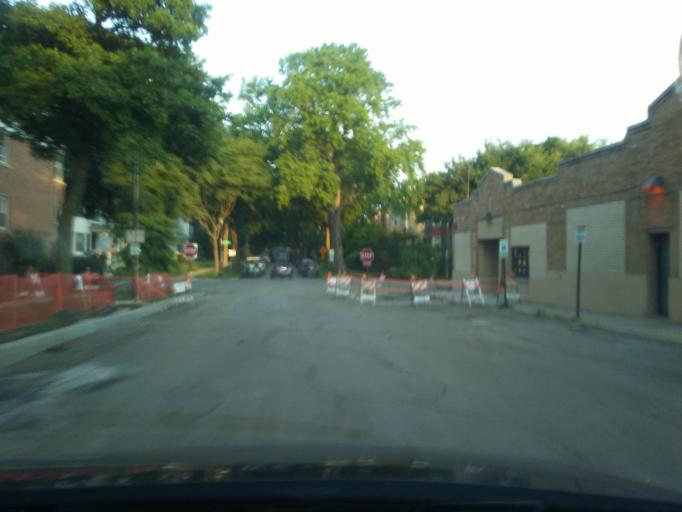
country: US
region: Illinois
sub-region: Cook County
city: Evanston
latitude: 42.0277
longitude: -87.6798
